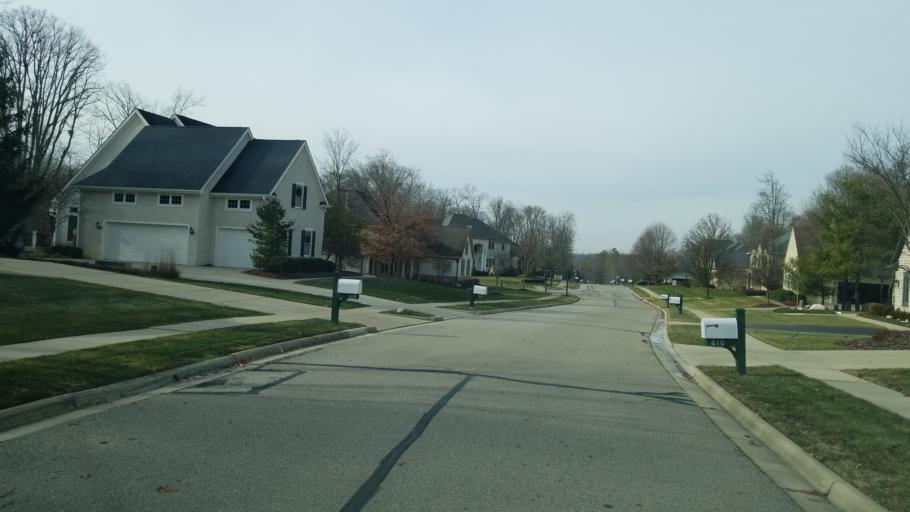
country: US
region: Ohio
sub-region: Delaware County
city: Lewis Center
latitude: 40.1679
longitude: -83.0330
